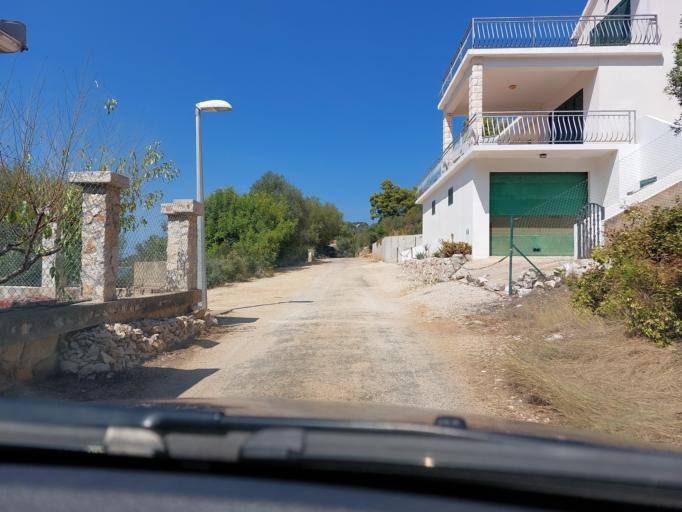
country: HR
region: Dubrovacko-Neretvanska
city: Smokvica
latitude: 42.7721
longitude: 16.8396
